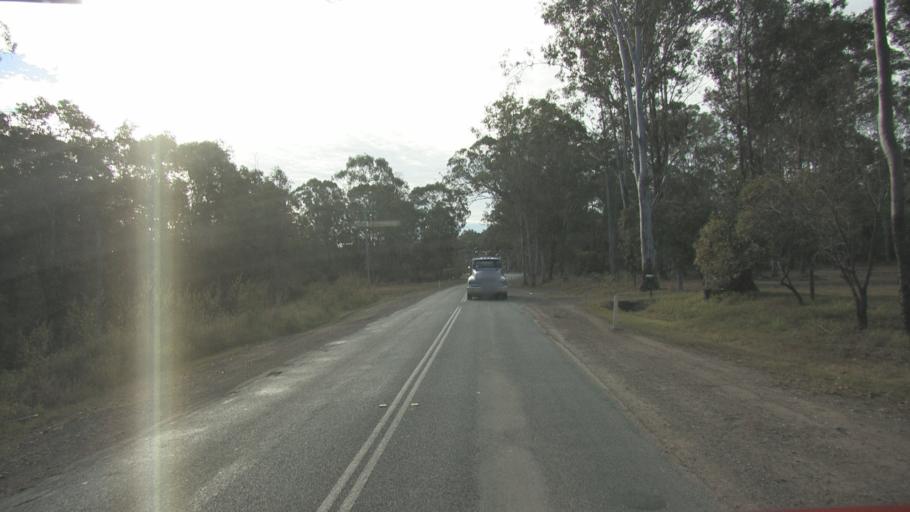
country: AU
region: Queensland
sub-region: Logan
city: Cedar Vale
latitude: -27.8489
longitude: 153.0510
